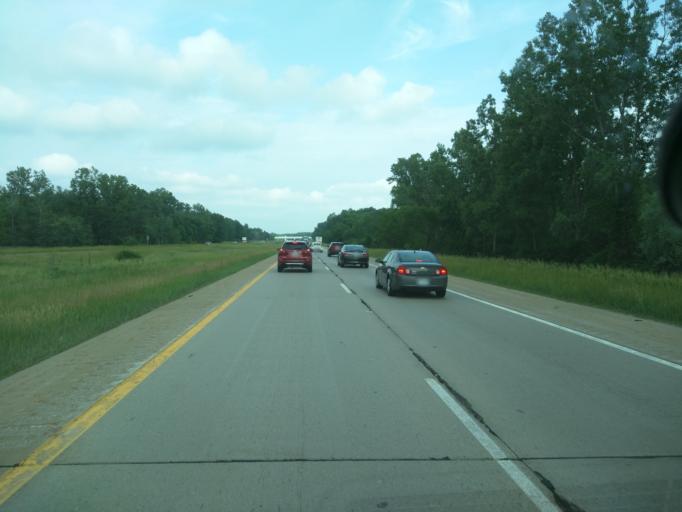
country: US
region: Michigan
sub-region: Clinton County
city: Bath
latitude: 42.8013
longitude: -84.4616
